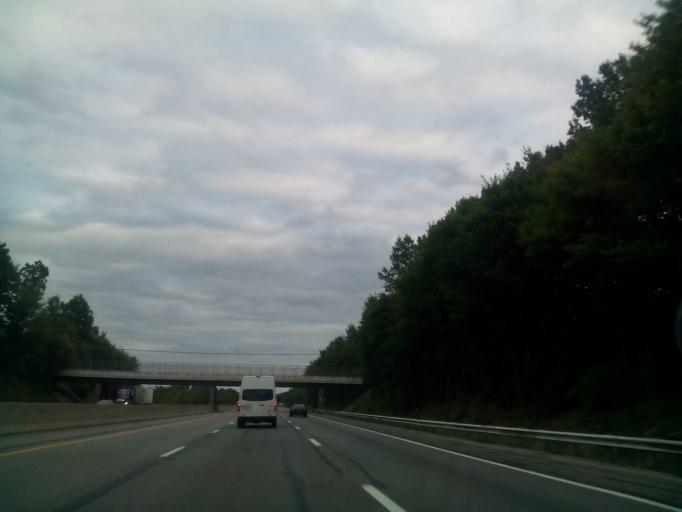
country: US
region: Ohio
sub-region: Portage County
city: Windham
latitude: 41.2416
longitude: -81.0317
